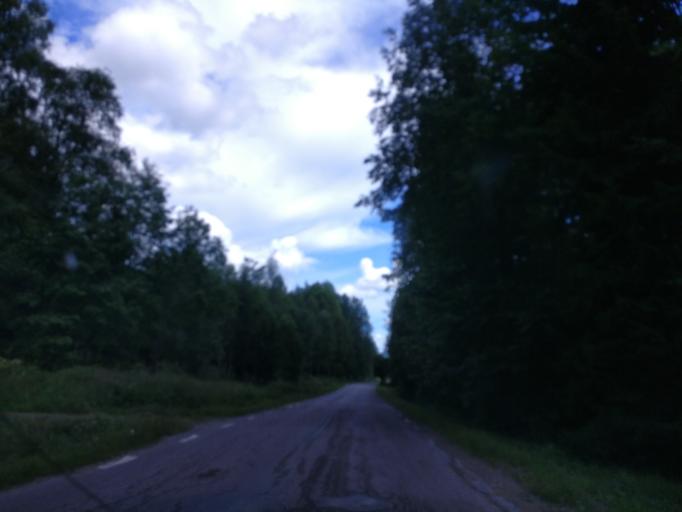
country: SE
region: Vaermland
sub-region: Hagfors Kommun
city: Ekshaerad
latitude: 60.1170
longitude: 13.4503
